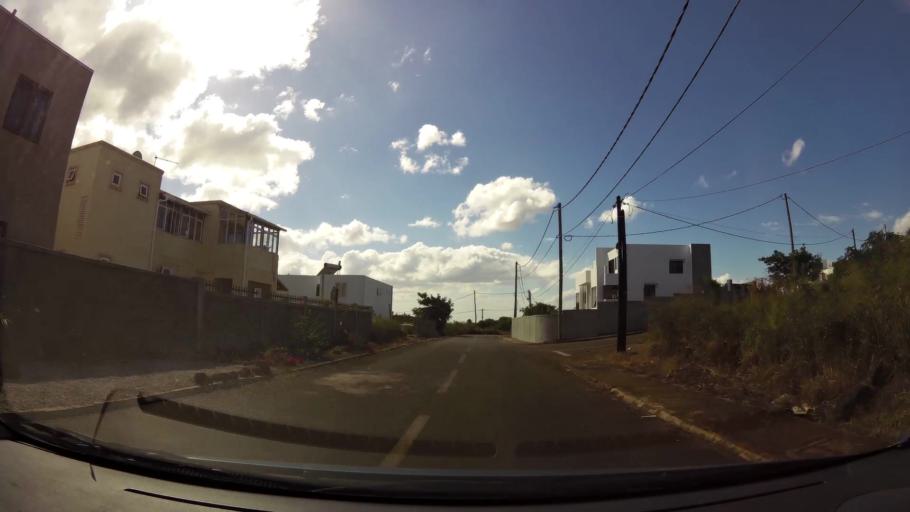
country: MU
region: Black River
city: Albion
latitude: -20.2224
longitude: 57.4166
